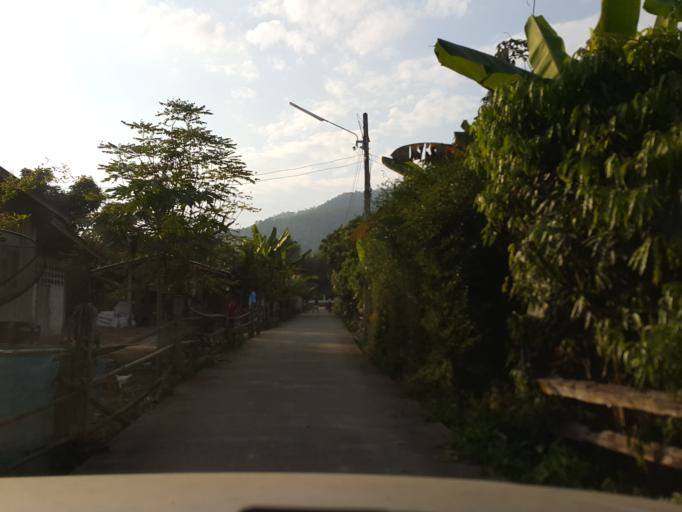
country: TH
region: Chiang Mai
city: Mae On
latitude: 18.6425
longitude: 99.2895
